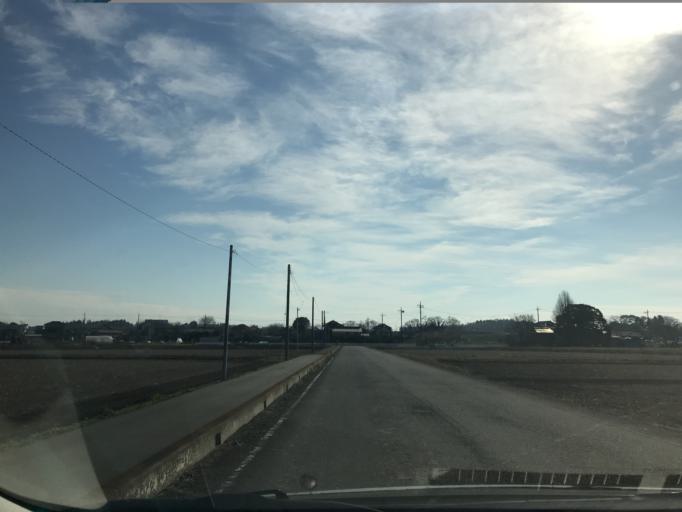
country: JP
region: Ibaraki
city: Mitsukaido
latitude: 36.0403
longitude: 140.0211
